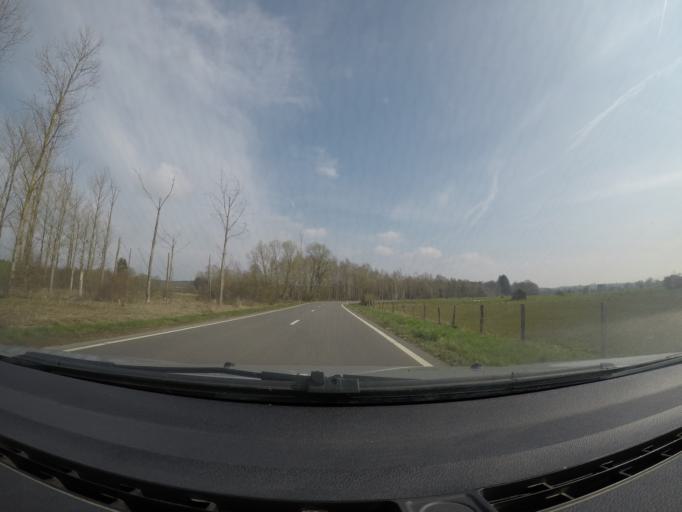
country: BE
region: Wallonia
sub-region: Province du Luxembourg
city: Tintigny
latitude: 49.7061
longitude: 5.4369
